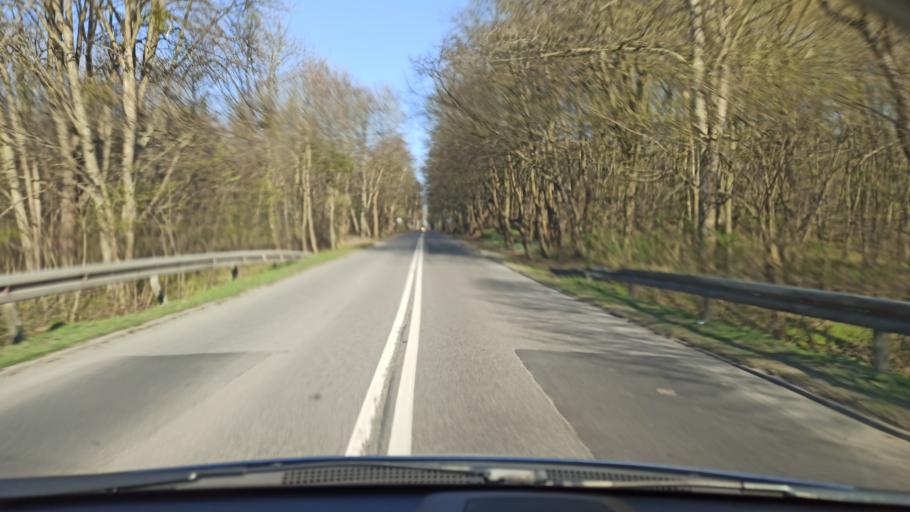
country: PL
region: Warmian-Masurian Voivodeship
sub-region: Powiat elblaski
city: Gronowo Gorne
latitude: 54.1844
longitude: 19.4494
